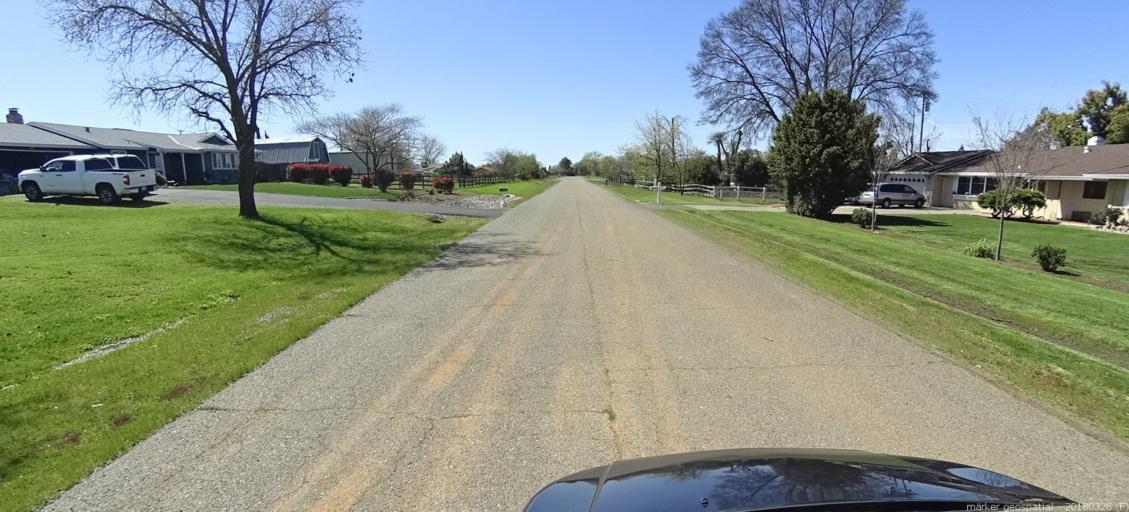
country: US
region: California
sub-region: Sacramento County
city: Wilton
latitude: 38.4811
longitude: -121.2318
